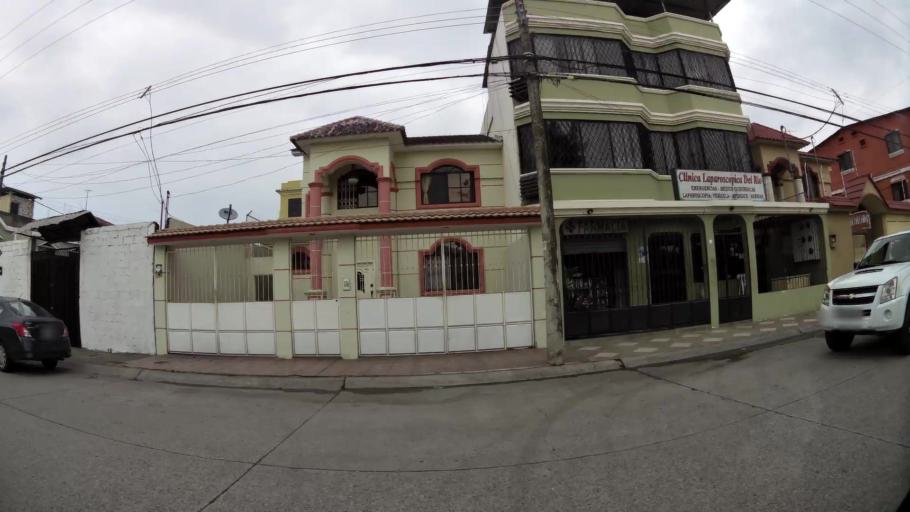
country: EC
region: Guayas
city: Eloy Alfaro
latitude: -2.1347
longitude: -79.8858
